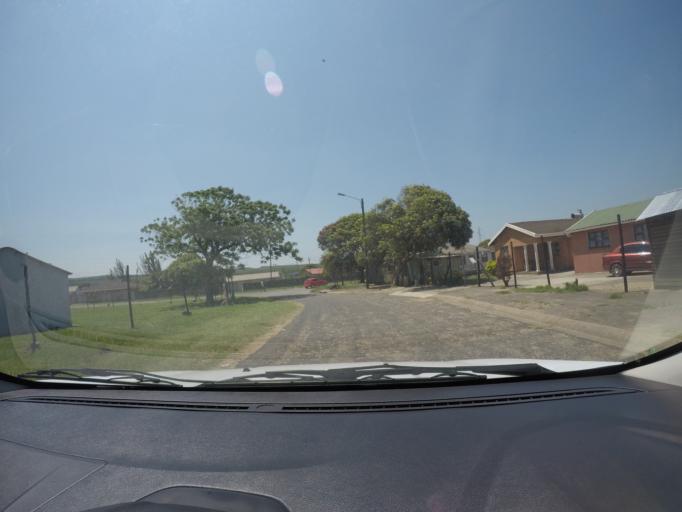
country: ZA
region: KwaZulu-Natal
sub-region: uThungulu District Municipality
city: eSikhawini
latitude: -28.8713
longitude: 31.9023
